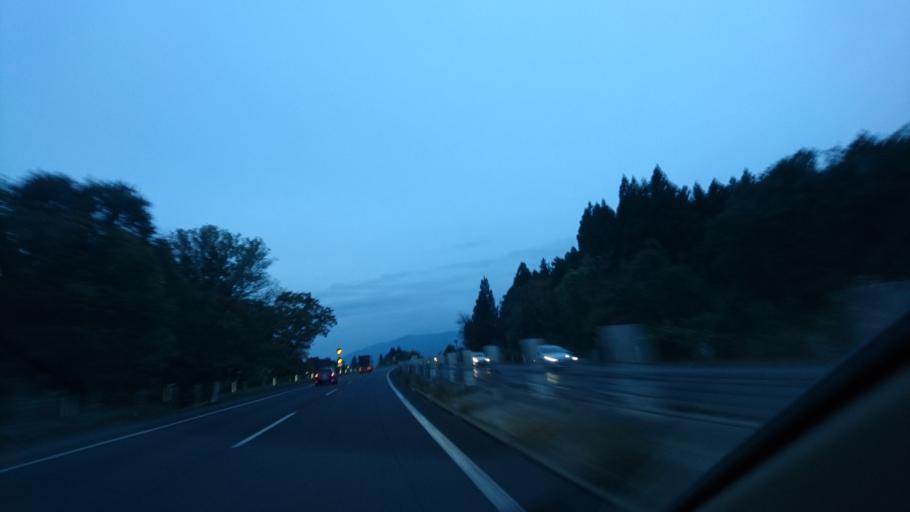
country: JP
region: Iwate
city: Morioka-shi
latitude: 39.6108
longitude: 141.1284
